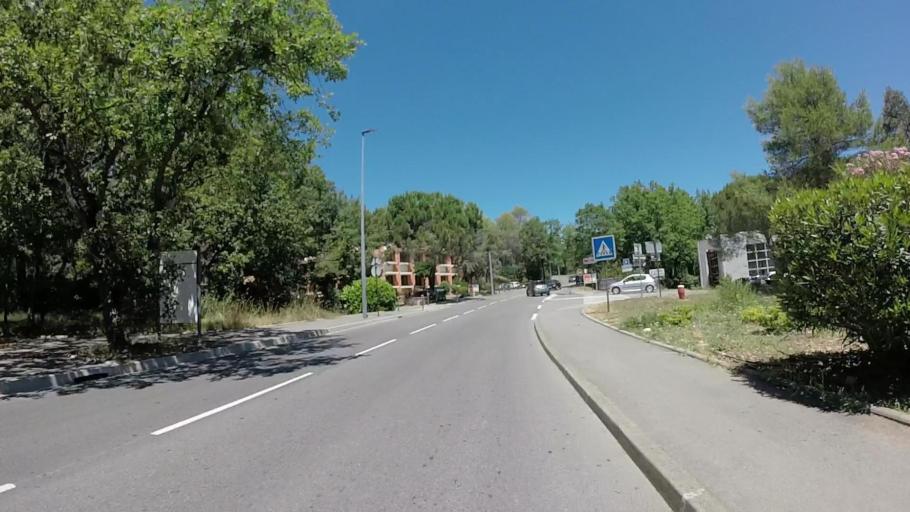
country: FR
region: Provence-Alpes-Cote d'Azur
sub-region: Departement des Alpes-Maritimes
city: Valbonne
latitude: 43.6244
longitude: 7.0445
